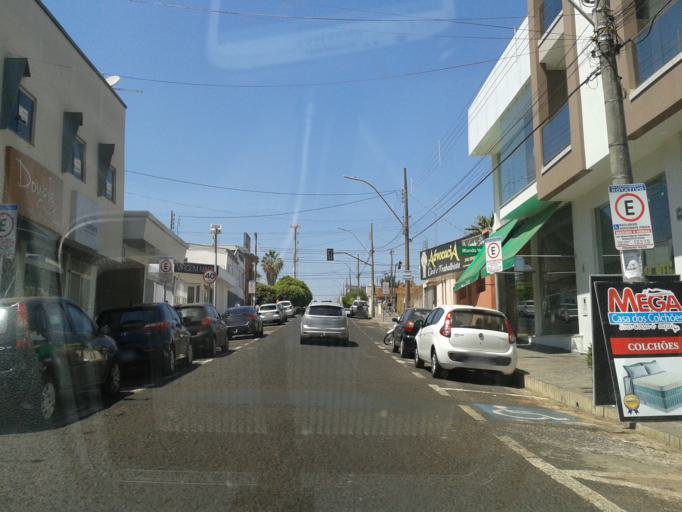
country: BR
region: Minas Gerais
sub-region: Araguari
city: Araguari
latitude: -18.6522
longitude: -48.1933
